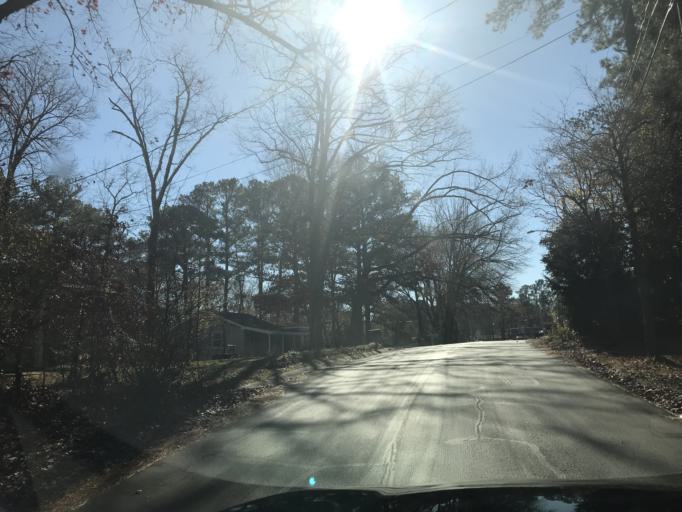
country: US
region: Georgia
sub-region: Clayton County
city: Morrow
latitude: 33.5746
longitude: -84.3691
